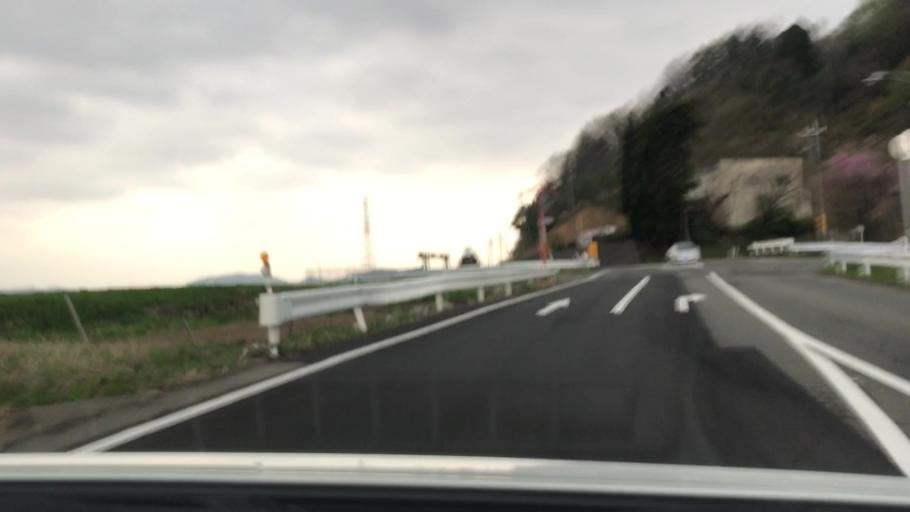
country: JP
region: Fukui
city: Fukui-shi
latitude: 36.0844
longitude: 136.1804
